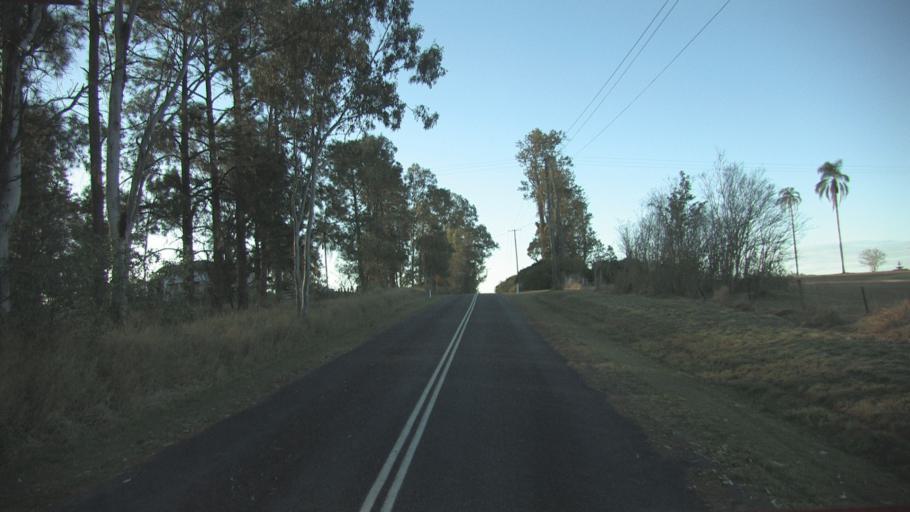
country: AU
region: Queensland
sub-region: Logan
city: Cedar Vale
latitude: -27.8623
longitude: 153.1223
